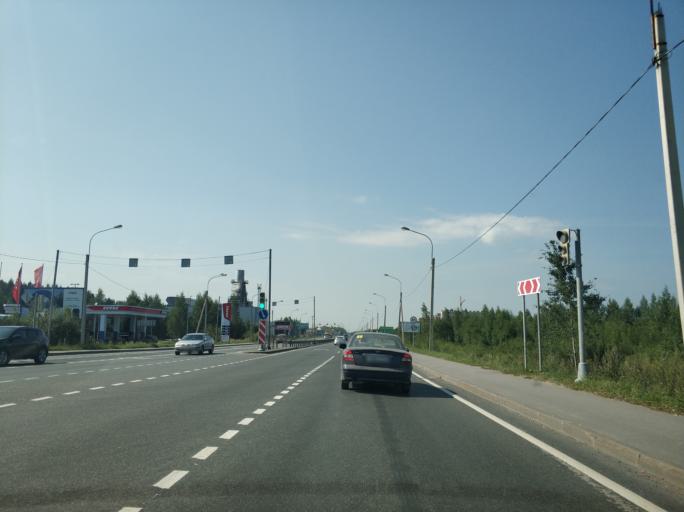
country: RU
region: Leningrad
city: Vsevolozhsk
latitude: 60.0270
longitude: 30.6164
